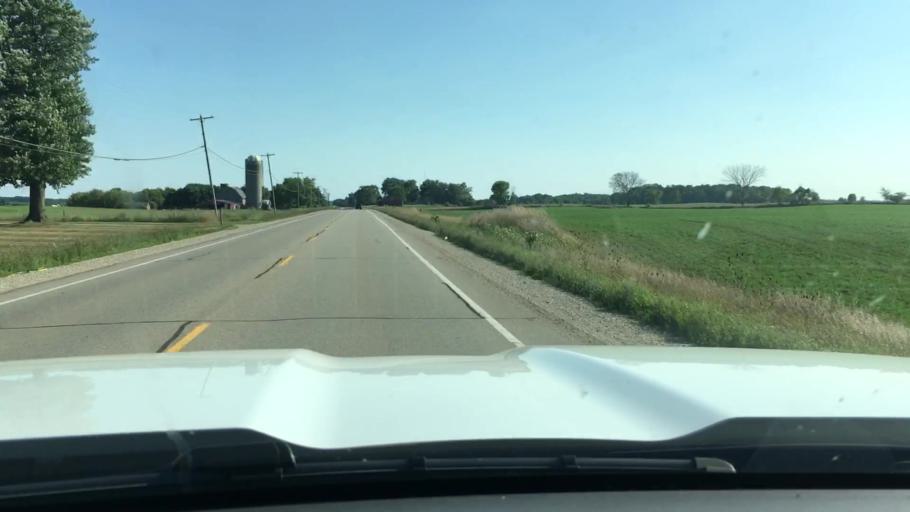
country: US
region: Michigan
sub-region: Ottawa County
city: Coopersville
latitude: 43.0349
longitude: -85.9567
